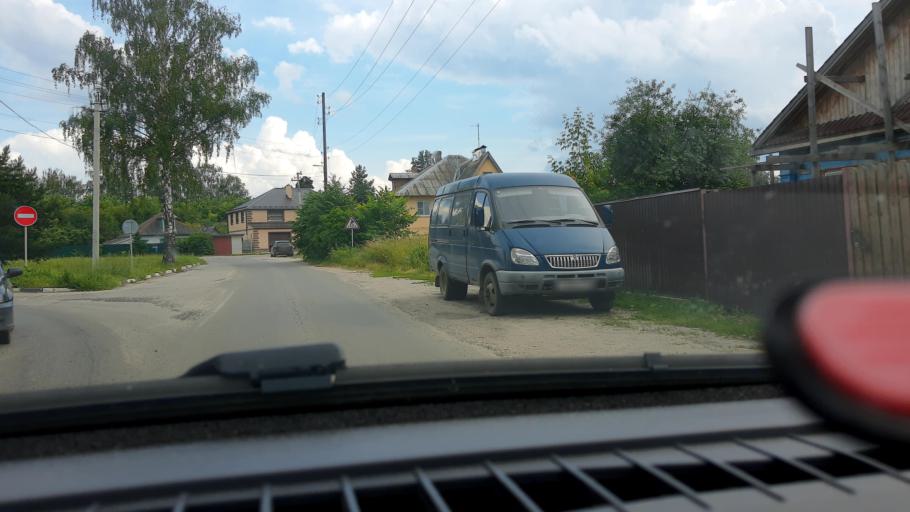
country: RU
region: Nizjnij Novgorod
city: Gorodets
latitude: 56.6354
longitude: 43.4751
